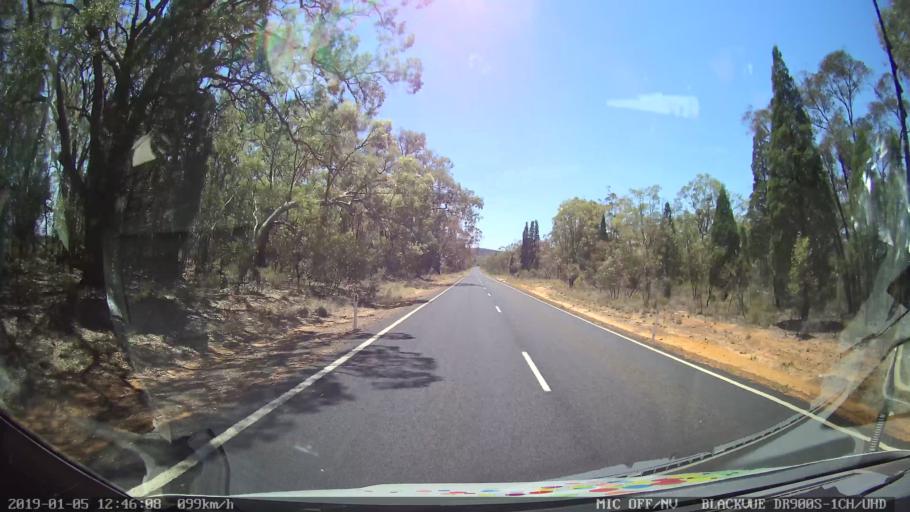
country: AU
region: New South Wales
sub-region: Warrumbungle Shire
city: Coonabarabran
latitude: -31.1210
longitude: 149.5587
